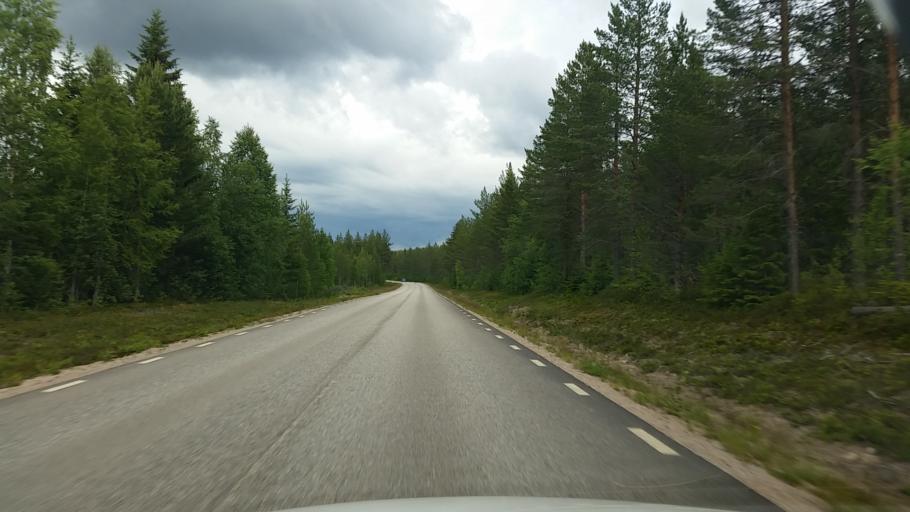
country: SE
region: Jaemtland
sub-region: Harjedalens Kommun
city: Sveg
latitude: 61.9806
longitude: 15.0798
